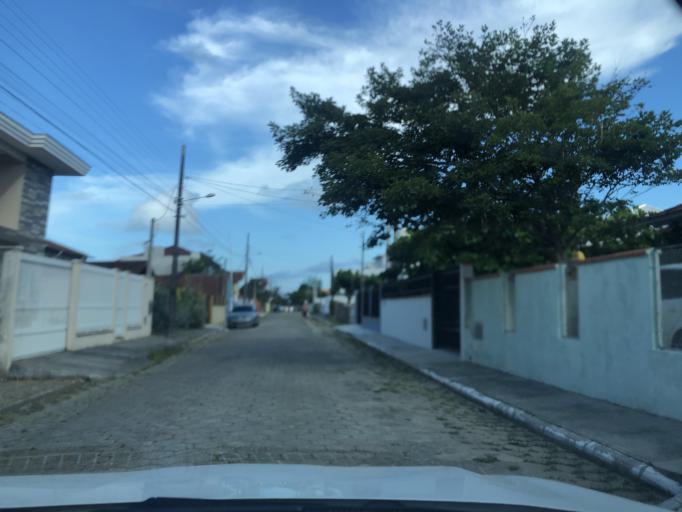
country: BR
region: Santa Catarina
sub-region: Sao Francisco Do Sul
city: Sao Francisco do Sul
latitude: -26.2274
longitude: -48.5151
